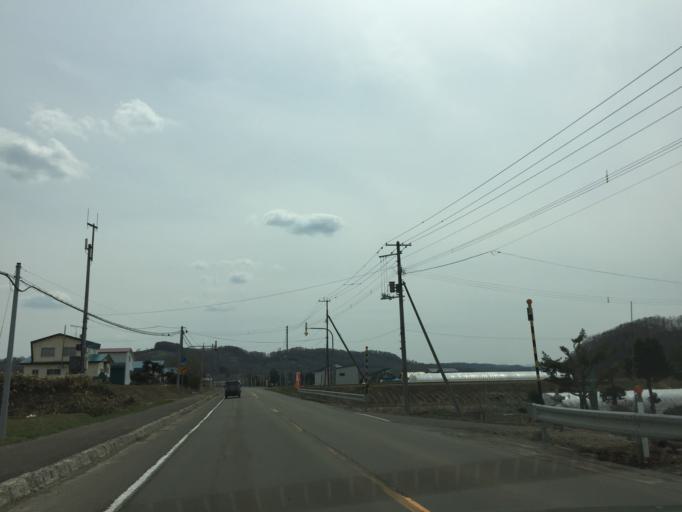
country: JP
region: Hokkaido
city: Ashibetsu
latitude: 43.6070
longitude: 142.2046
